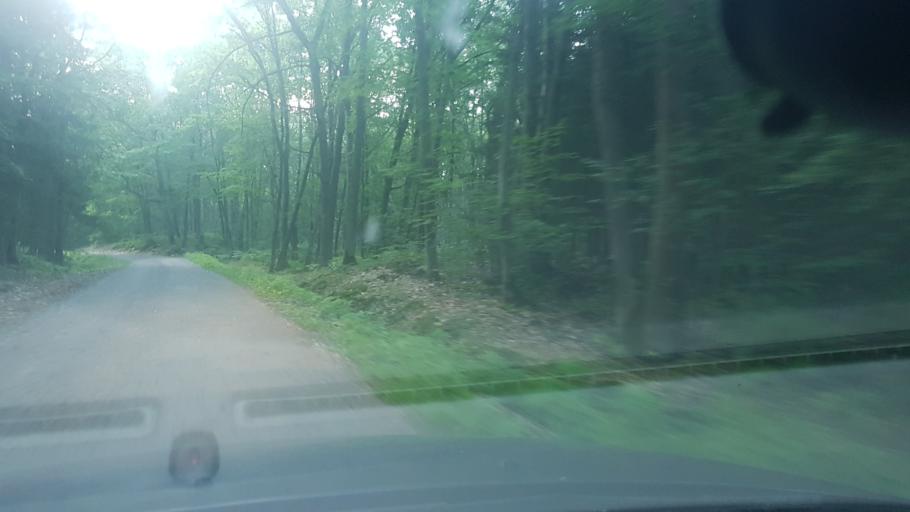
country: PL
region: Pomeranian Voivodeship
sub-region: Powiat nowodworski
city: Krynica Morska
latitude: 54.3568
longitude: 19.3428
